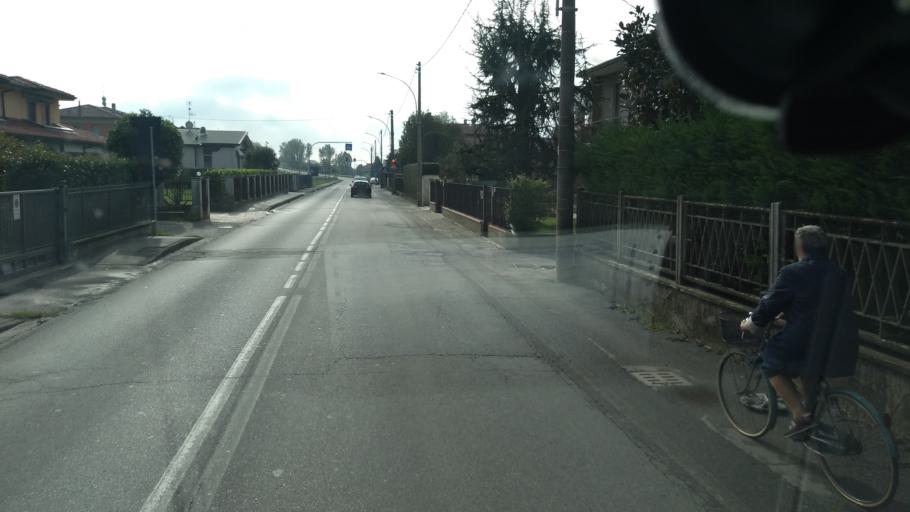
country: IT
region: Lombardy
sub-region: Provincia di Bergamo
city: Vidalengo
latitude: 45.5225
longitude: 9.6394
